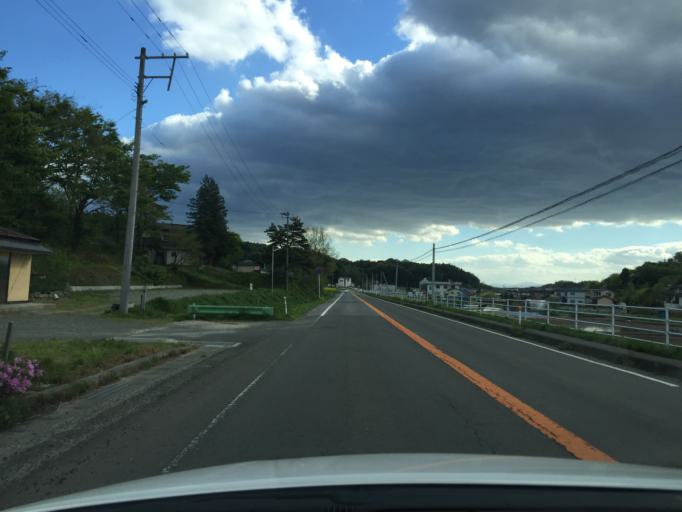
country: JP
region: Fukushima
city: Fukushima-shi
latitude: 37.6696
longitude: 140.5568
